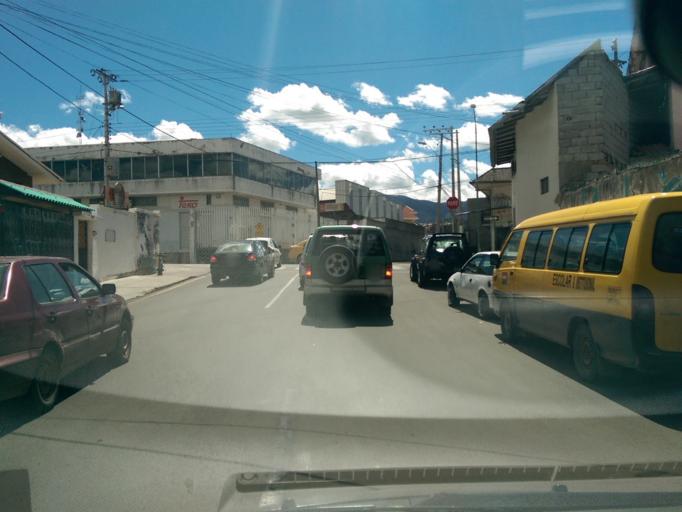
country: EC
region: Azuay
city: Cuenca
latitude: -2.9012
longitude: -79.0147
